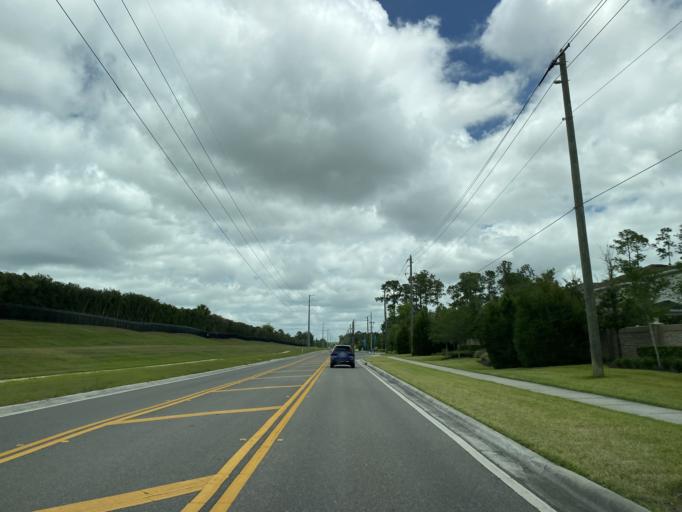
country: US
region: Florida
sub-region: Seminole County
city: Lake Mary
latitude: 28.8193
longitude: -81.3392
